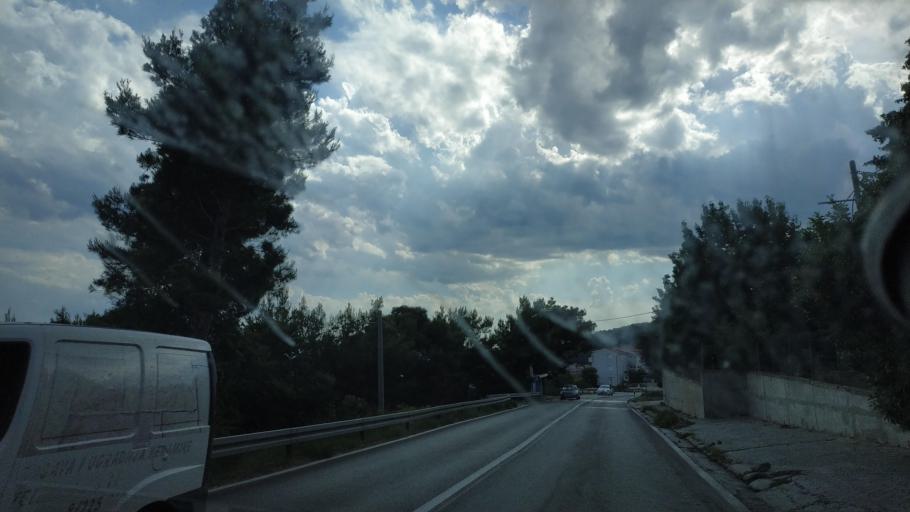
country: HR
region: Splitsko-Dalmatinska
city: Klis
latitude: 43.5566
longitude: 16.5062
